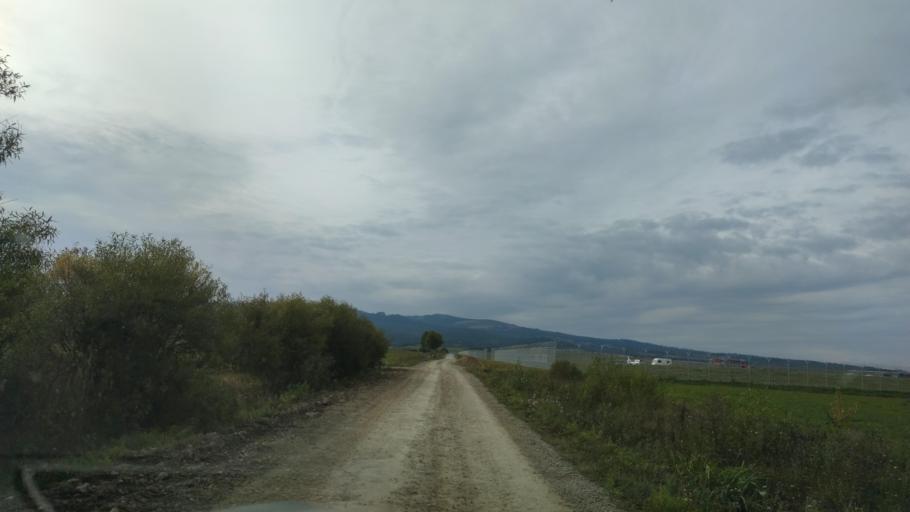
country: RO
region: Harghita
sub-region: Comuna Subcetate
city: Subcetate
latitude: 46.8170
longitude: 25.4145
